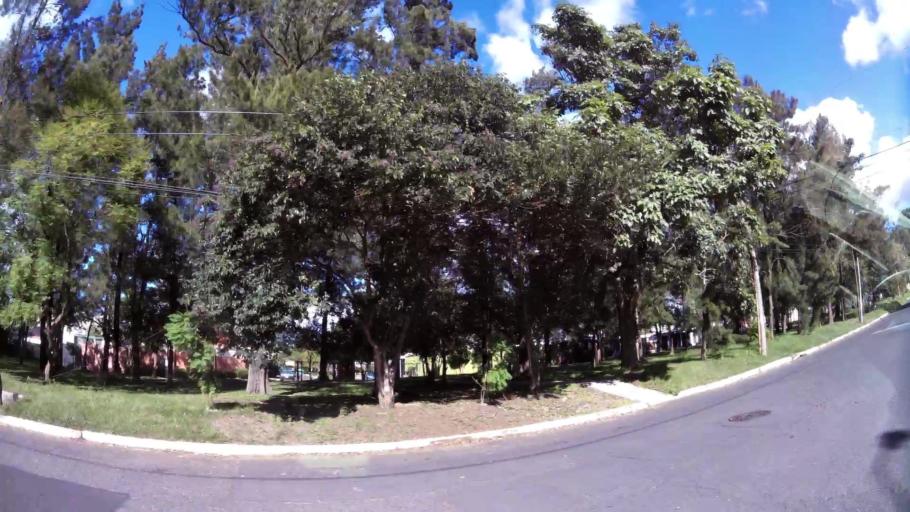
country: GT
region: Guatemala
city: Mixco
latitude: 14.6050
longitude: -90.5585
